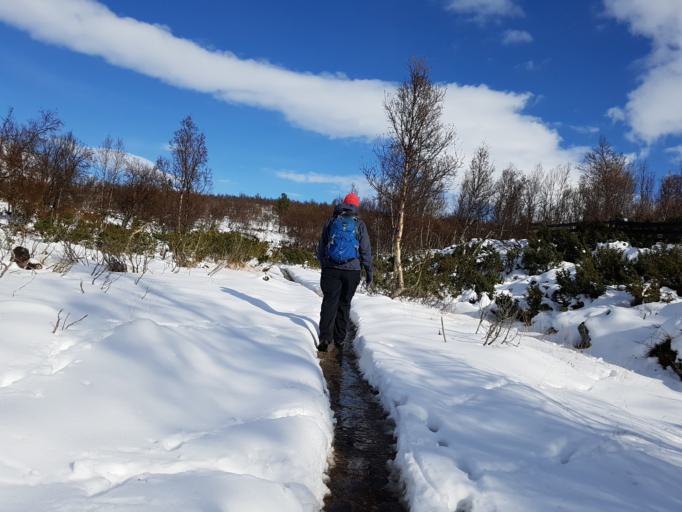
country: NO
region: Oppland
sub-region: Sel
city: Otta
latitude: 61.8264
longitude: 9.6823
